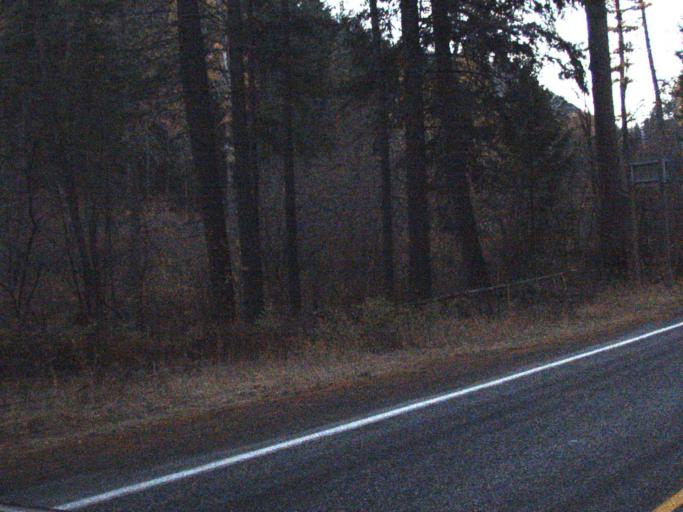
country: US
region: Washington
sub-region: Ferry County
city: Republic
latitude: 48.5172
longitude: -118.7388
